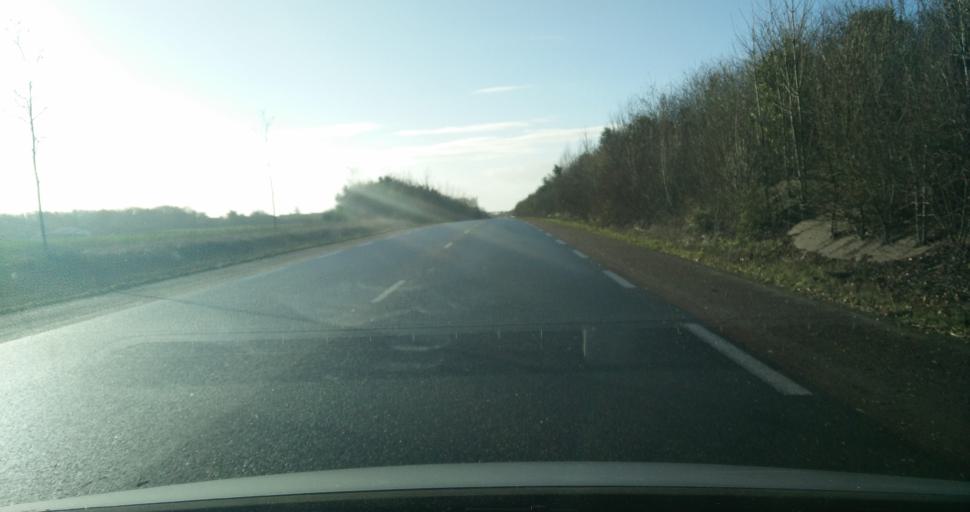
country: FR
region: Poitou-Charentes
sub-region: Departement de la Charente-Maritime
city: Saint-Xandre
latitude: 46.1926
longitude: -1.0947
